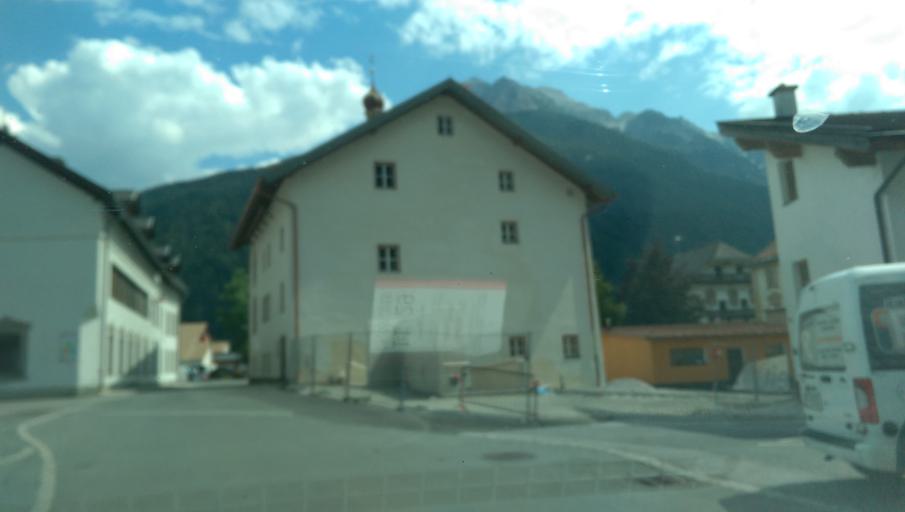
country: AT
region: Tyrol
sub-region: Politischer Bezirk Innsbruck Land
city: Fulpmes
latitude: 47.1535
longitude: 11.3473
